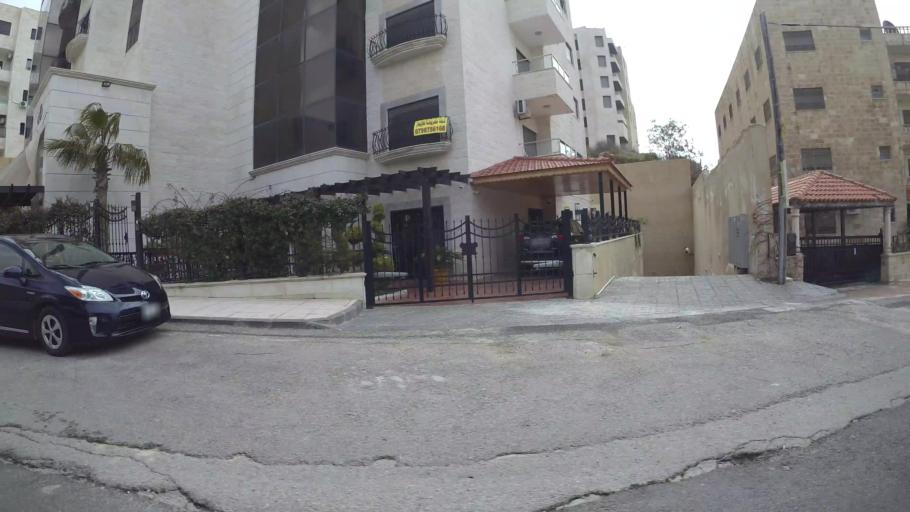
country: JO
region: Amman
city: Al Jubayhah
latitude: 32.0020
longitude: 35.8412
